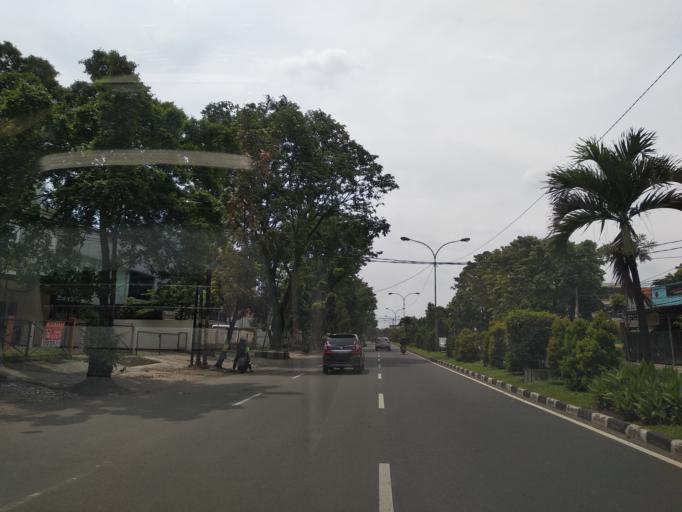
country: ID
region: West Java
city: Bandung
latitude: -6.9379
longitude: 107.6152
